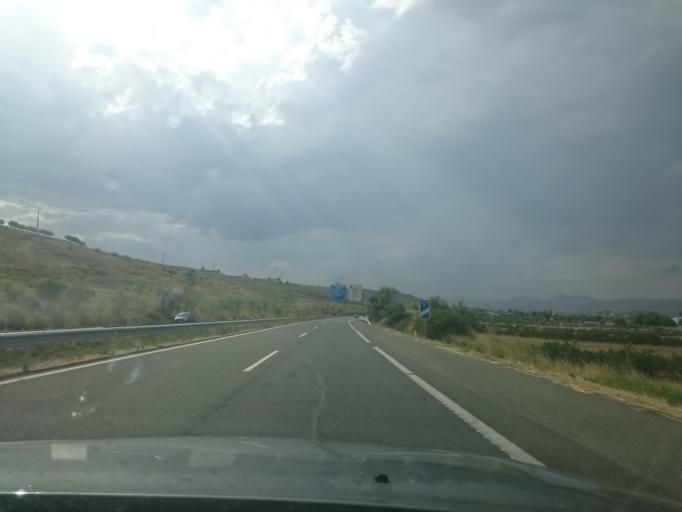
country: ES
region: La Rioja
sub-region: Provincia de La Rioja
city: Agoncillo
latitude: 42.4319
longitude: -2.2843
